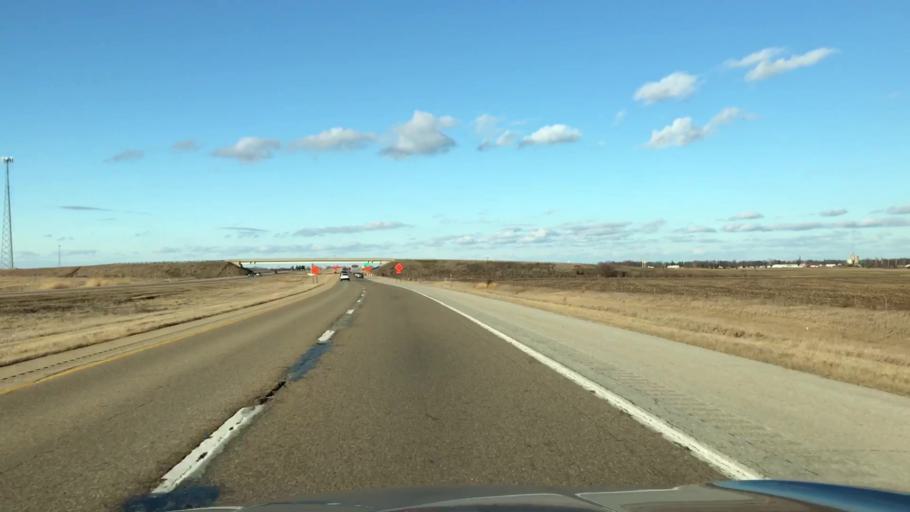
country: US
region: Illinois
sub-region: McLean County
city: Chenoa
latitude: 40.7232
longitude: -88.7370
